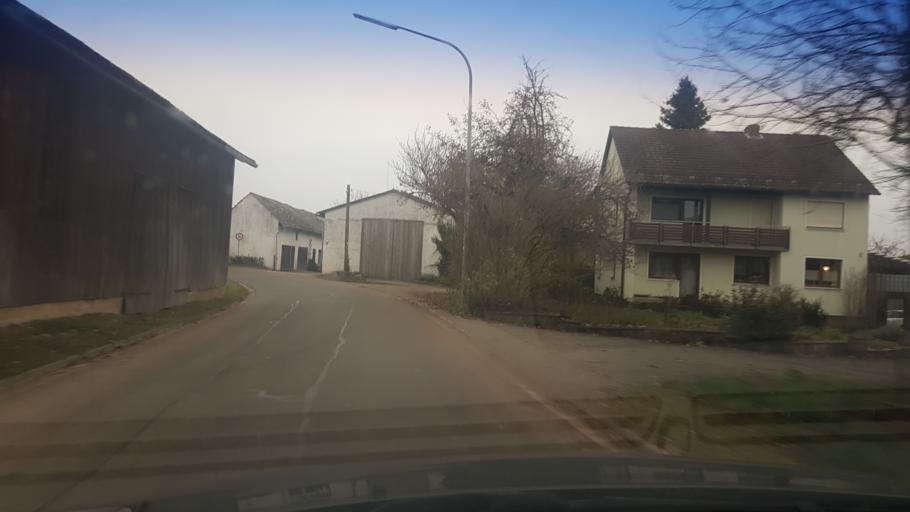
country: DE
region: Bavaria
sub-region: Upper Franconia
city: Kasendorf
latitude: 50.0356
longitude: 11.2922
